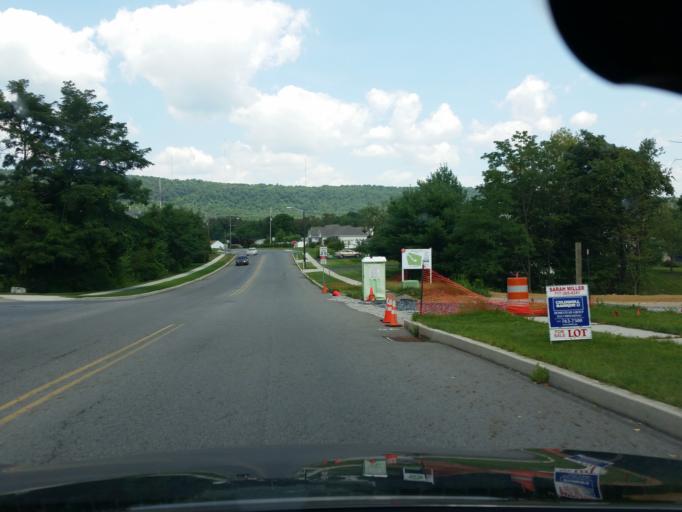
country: US
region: Pennsylvania
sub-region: Cumberland County
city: Enola
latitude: 40.2934
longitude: -76.9491
